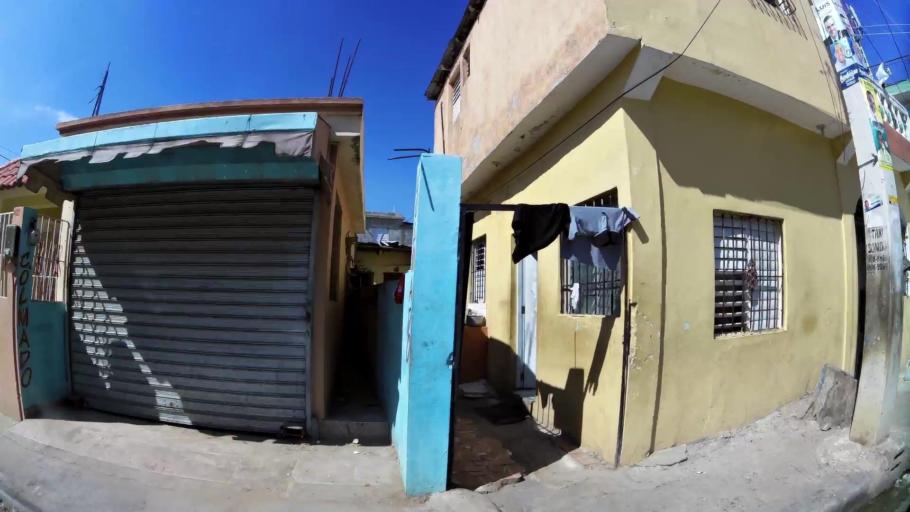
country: DO
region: Santo Domingo
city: Santo Domingo Oeste
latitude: 18.4723
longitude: -70.0048
